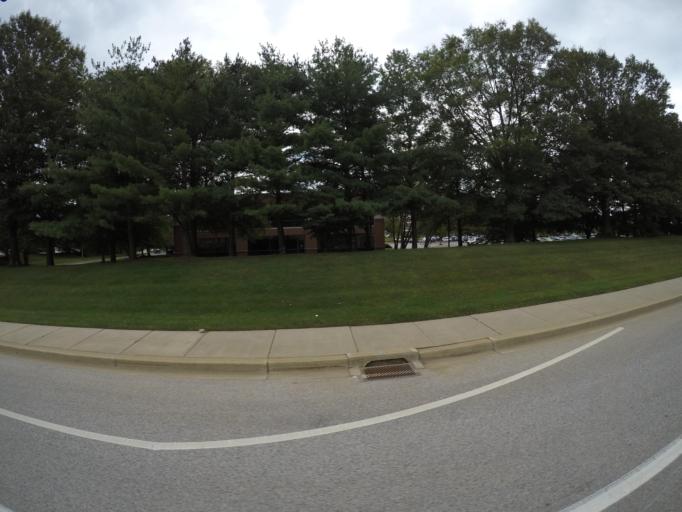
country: US
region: Delaware
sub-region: New Castle County
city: Brookside
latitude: 39.6798
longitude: -75.7314
